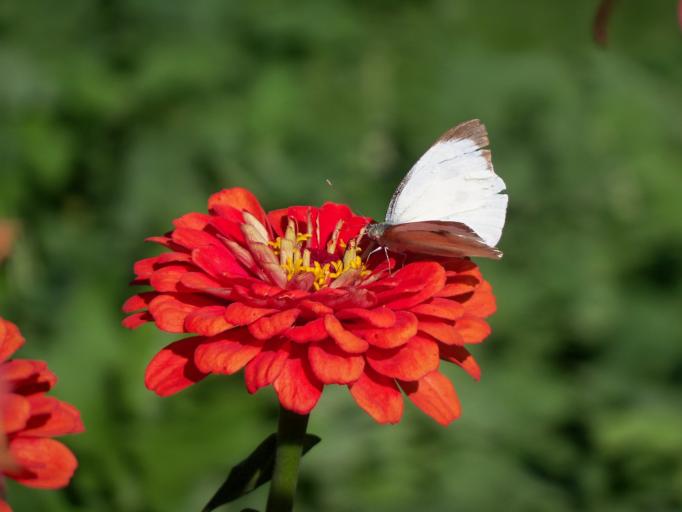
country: CZ
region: Vysocina
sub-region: Okres Jihlava
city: Telc
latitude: 49.1855
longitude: 15.4646
